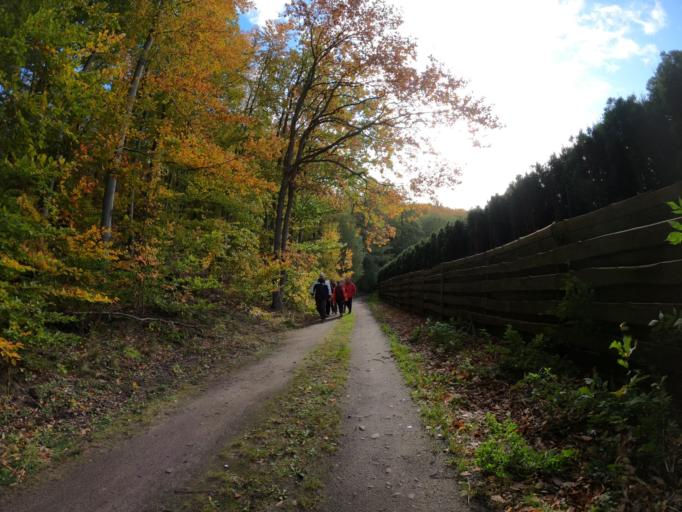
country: PL
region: West Pomeranian Voivodeship
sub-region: Powiat mysliborski
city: Barlinek
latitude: 52.9778
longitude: 15.2269
